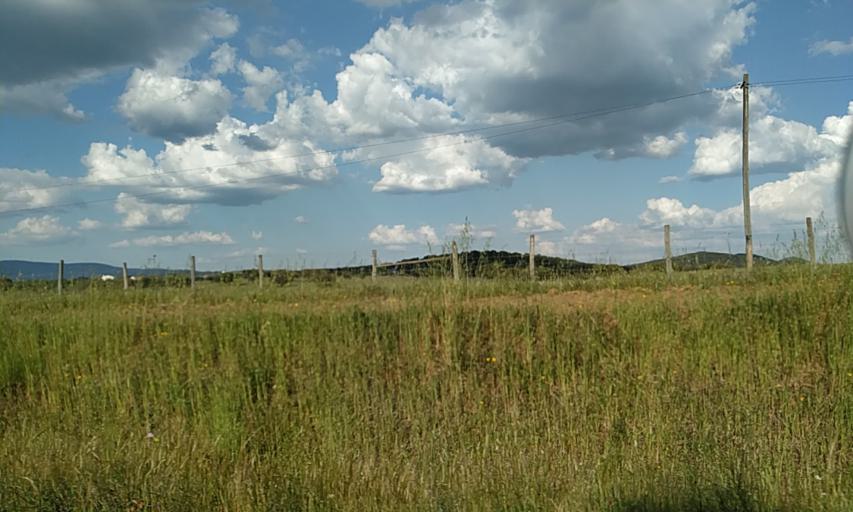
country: PT
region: Portalegre
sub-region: Portalegre
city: Urra
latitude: 39.2030
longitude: -7.4585
